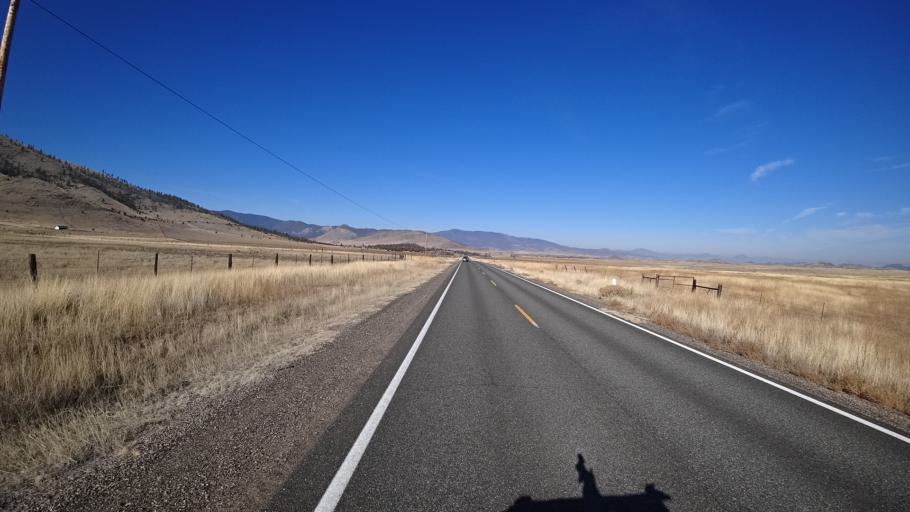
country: US
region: California
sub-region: Siskiyou County
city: Weed
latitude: 41.4826
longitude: -122.4968
